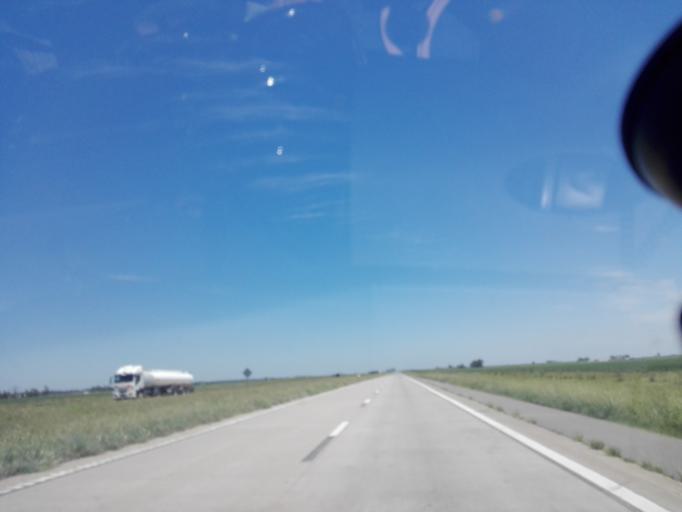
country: AR
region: Cordoba
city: Marcos Juarez
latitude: -32.6535
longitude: -62.1565
